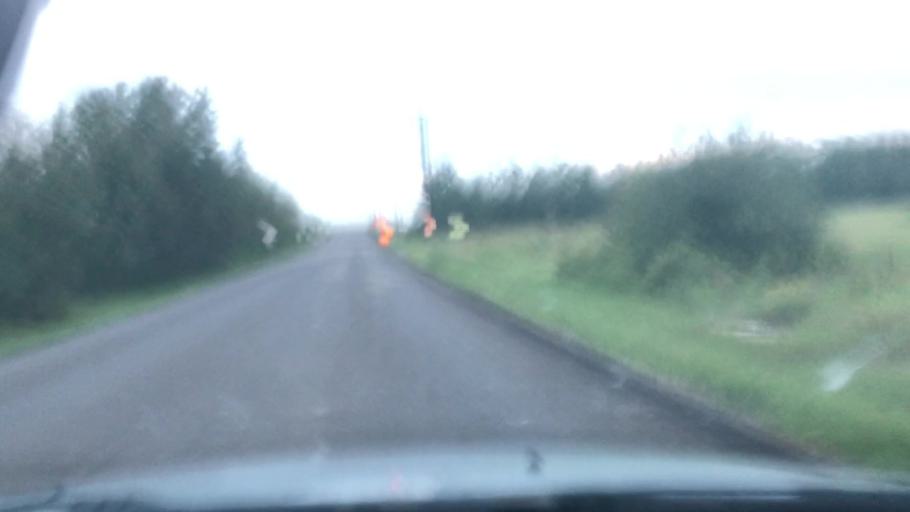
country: CA
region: Alberta
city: Devon
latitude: 53.4818
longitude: -113.6890
